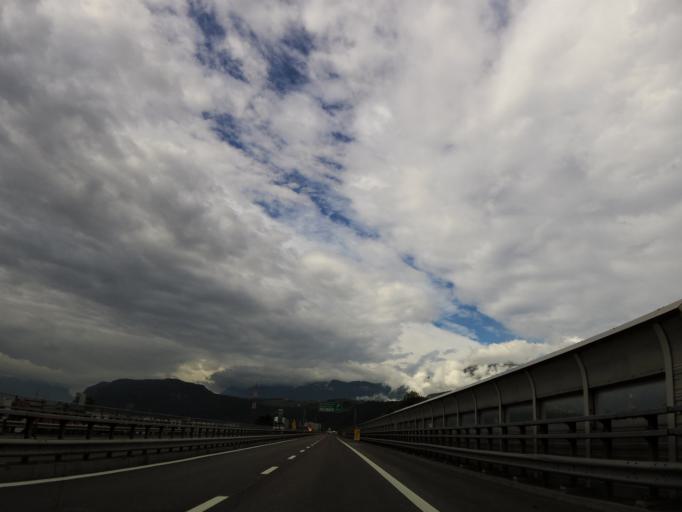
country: IT
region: Trentino-Alto Adige
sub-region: Bolzano
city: Bolzano
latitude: 46.4841
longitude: 11.3263
